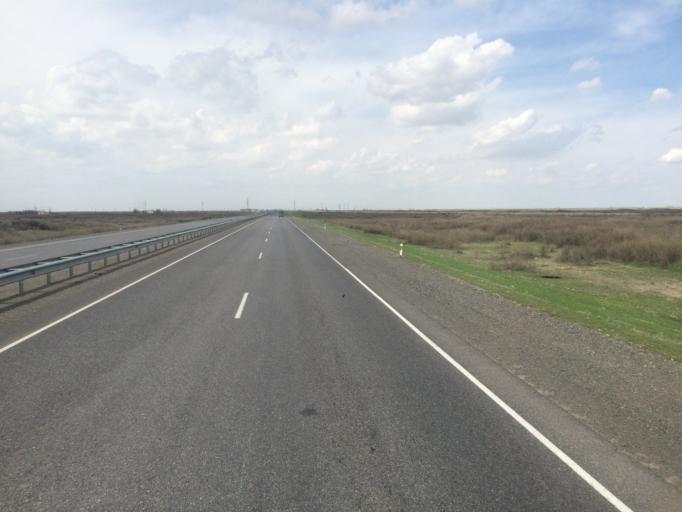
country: KZ
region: Qyzylorda
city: Zhangaqorghan
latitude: 43.9957
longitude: 67.2260
